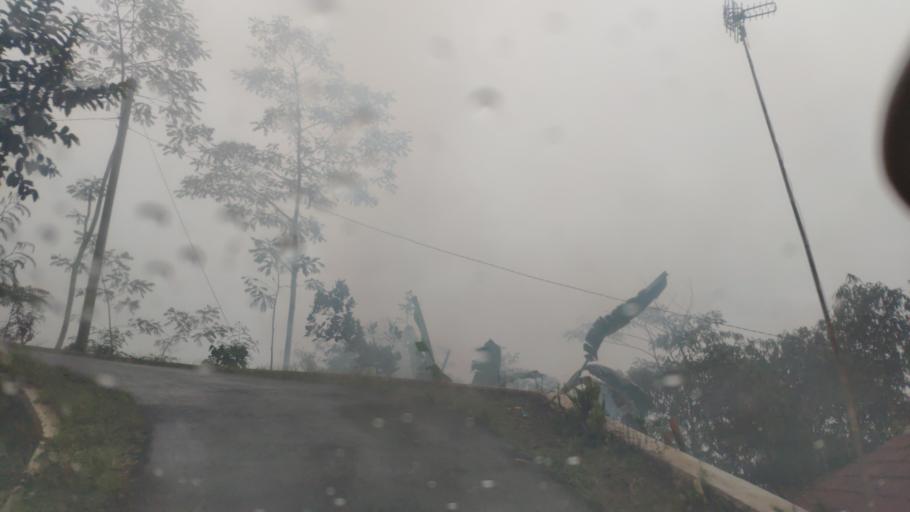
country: ID
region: Central Java
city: Wonosobo
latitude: -7.2833
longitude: 109.7272
